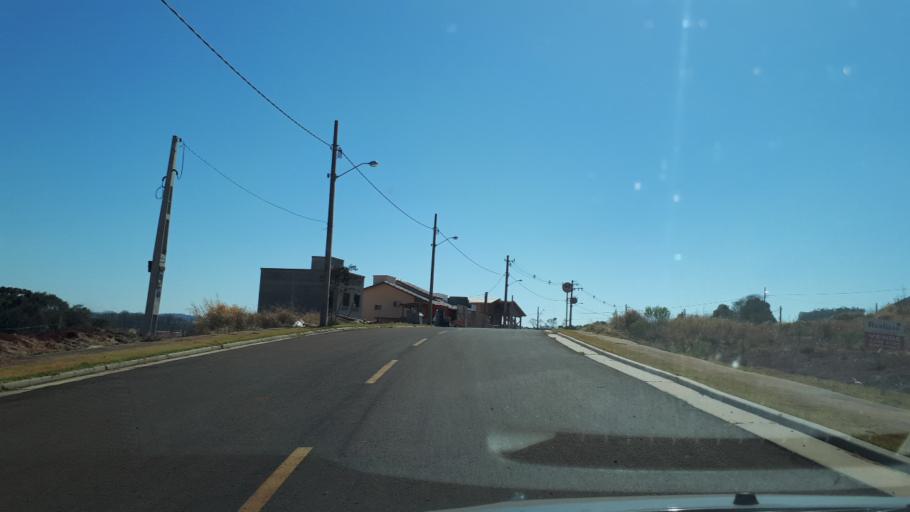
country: BR
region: Santa Catarina
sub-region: Chapeco
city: Chapeco
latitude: -27.0907
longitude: -52.7166
